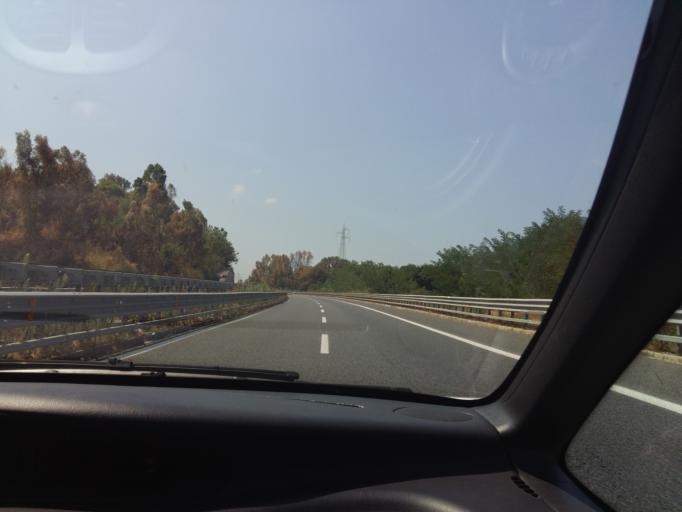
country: IT
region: Calabria
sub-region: Provincia di Reggio Calabria
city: Rosarno
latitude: 38.4972
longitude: 16.0157
